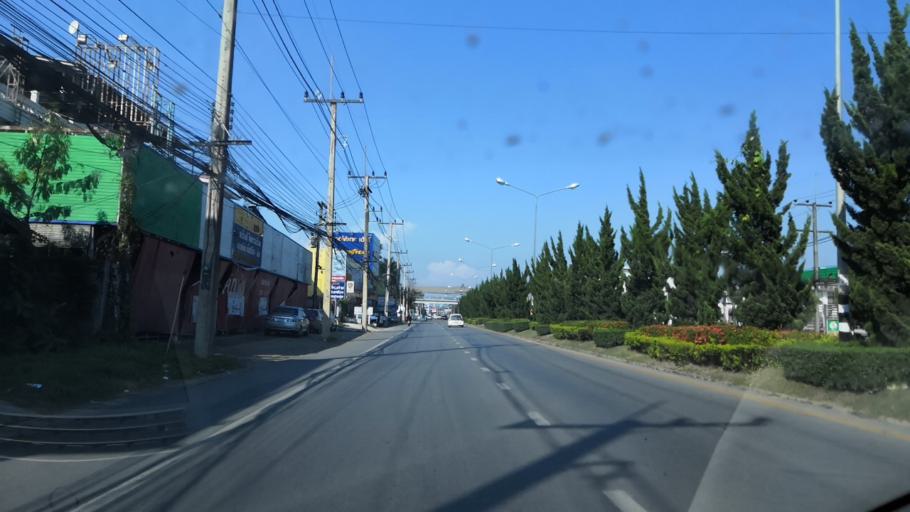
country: TH
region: Chiang Rai
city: Chiang Rai
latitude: 19.9331
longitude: 99.8447
